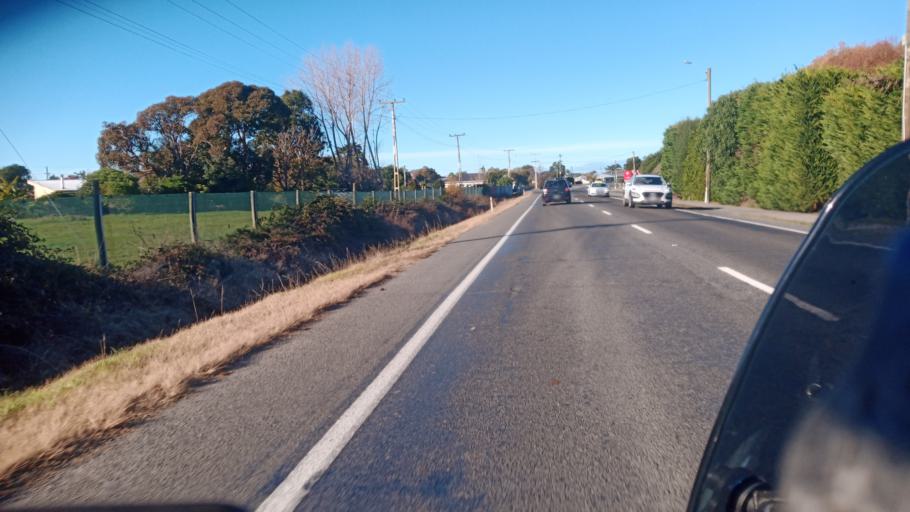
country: NZ
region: Hawke's Bay
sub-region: Napier City
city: Napier
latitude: -39.4274
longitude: 176.8712
